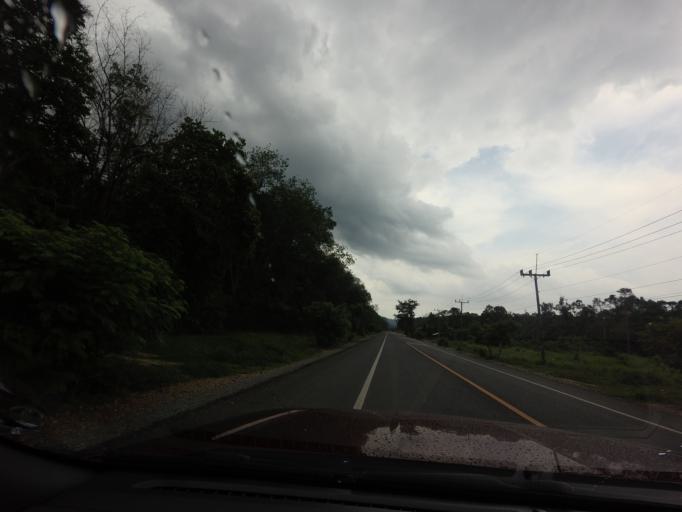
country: TH
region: Yala
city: Ban Nang Sata
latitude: 6.2333
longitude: 101.2149
